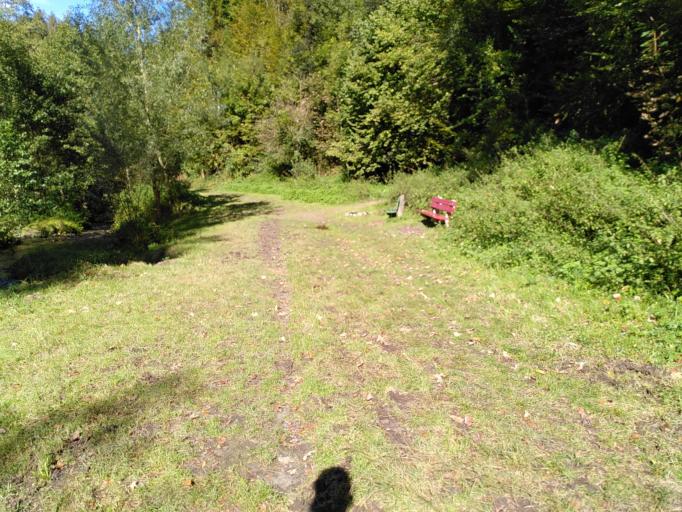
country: CH
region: Bern
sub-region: Oberaargau
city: Seeberg
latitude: 47.1307
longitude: 7.7053
